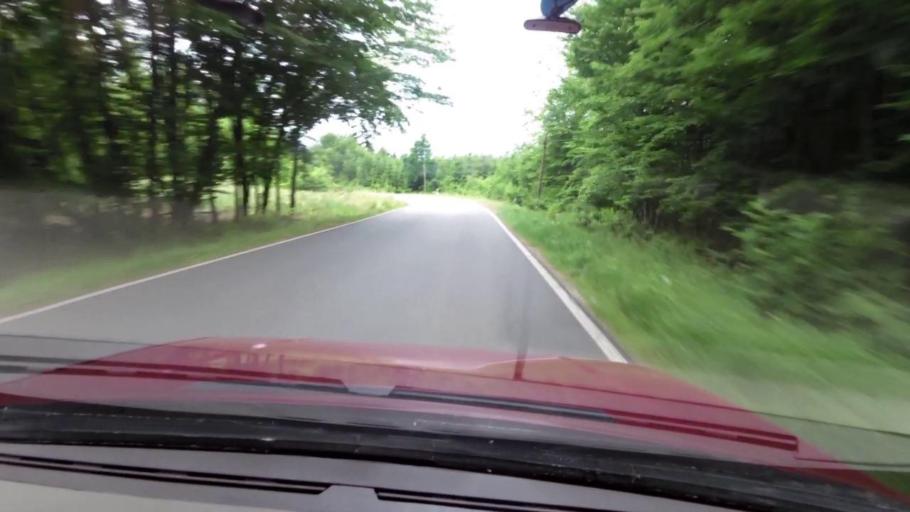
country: PL
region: West Pomeranian Voivodeship
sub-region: Powiat koszalinski
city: Polanow
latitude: 54.1552
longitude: 16.7010
